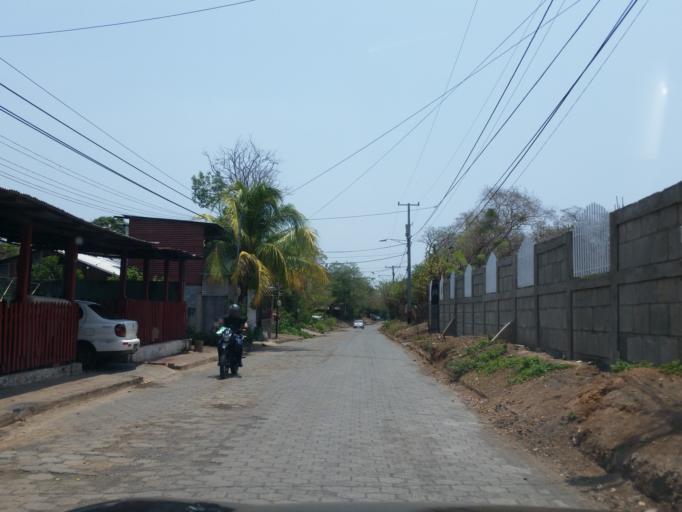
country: NI
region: Granada
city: Granada
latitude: 11.9295
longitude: -85.9691
